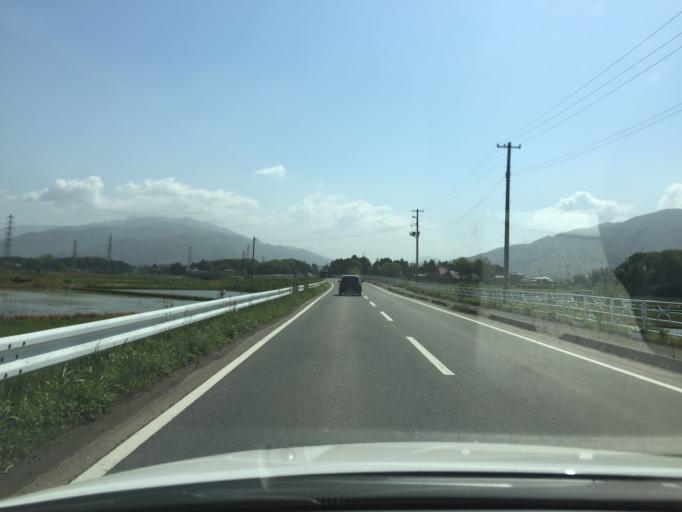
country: JP
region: Niigata
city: Gosen
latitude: 37.7333
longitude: 139.2246
